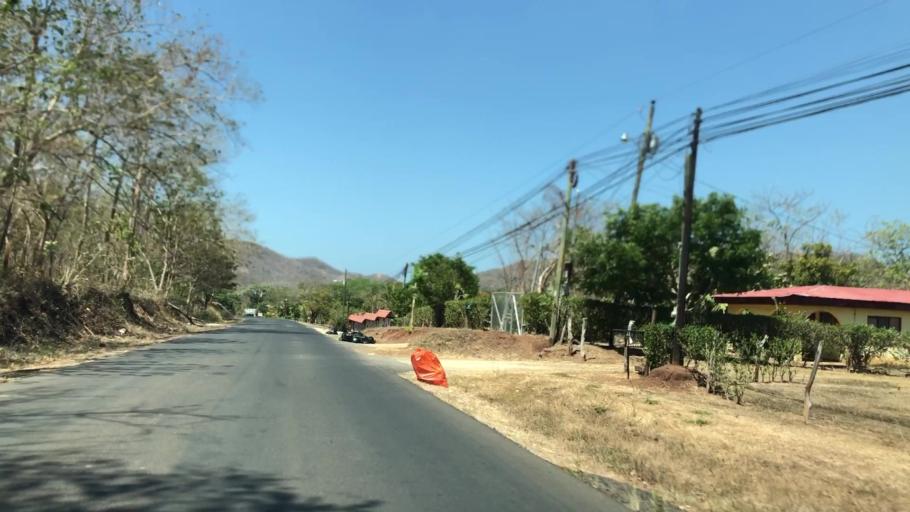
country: CR
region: Guanacaste
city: Sardinal
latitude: 10.3653
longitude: -85.8028
